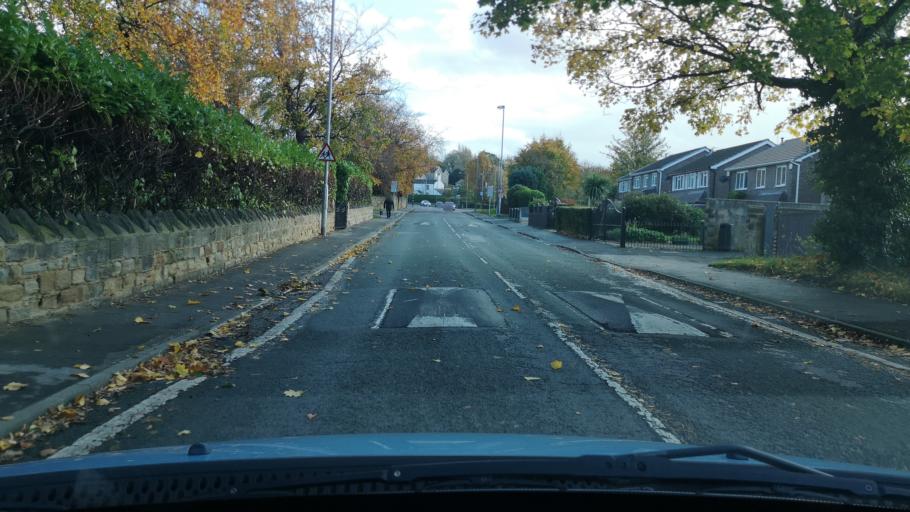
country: GB
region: England
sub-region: City and Borough of Wakefield
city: Crofton
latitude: 53.6606
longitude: -1.4346
